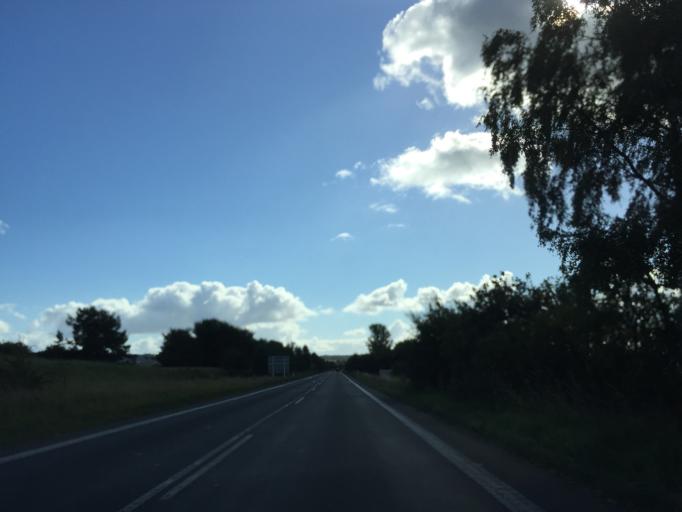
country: DK
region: Central Jutland
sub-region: Viborg Kommune
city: Bjerringbro
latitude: 56.3849
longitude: 9.6736
